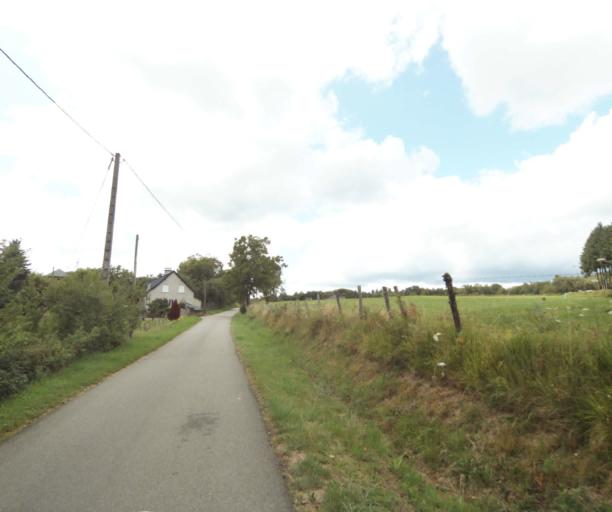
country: FR
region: Limousin
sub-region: Departement de la Correze
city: Sainte-Fortunade
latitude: 45.1817
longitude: 1.8225
